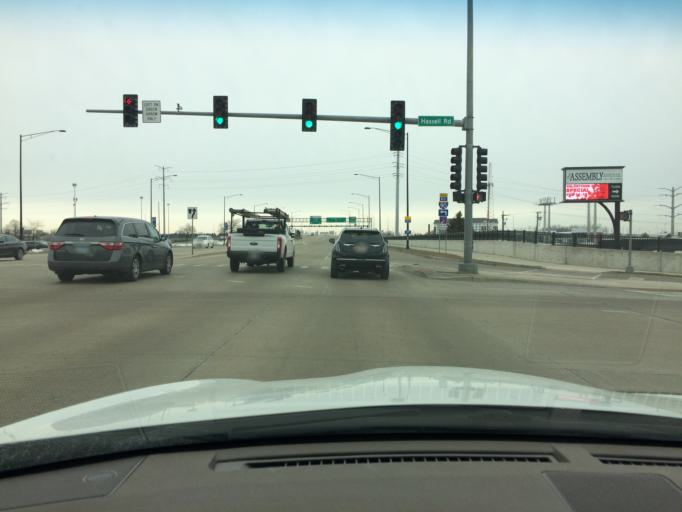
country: US
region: Illinois
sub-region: Cook County
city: South Barrington
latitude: 42.0626
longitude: -88.1444
